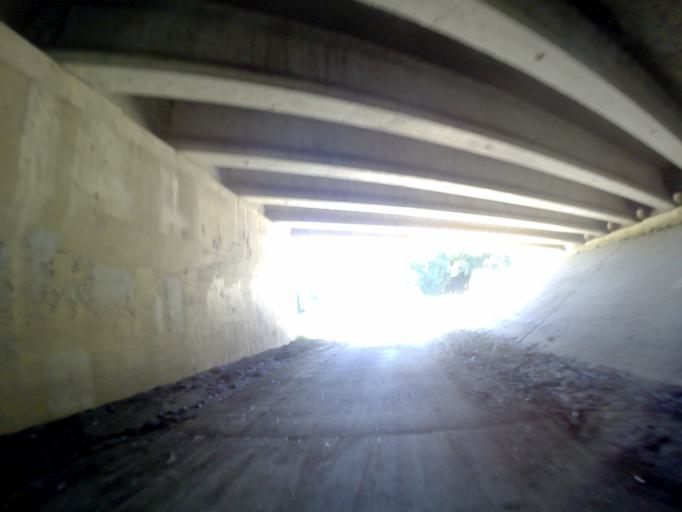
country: US
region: Illinois
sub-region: DuPage County
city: Warrenville
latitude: 41.8059
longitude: -88.1761
